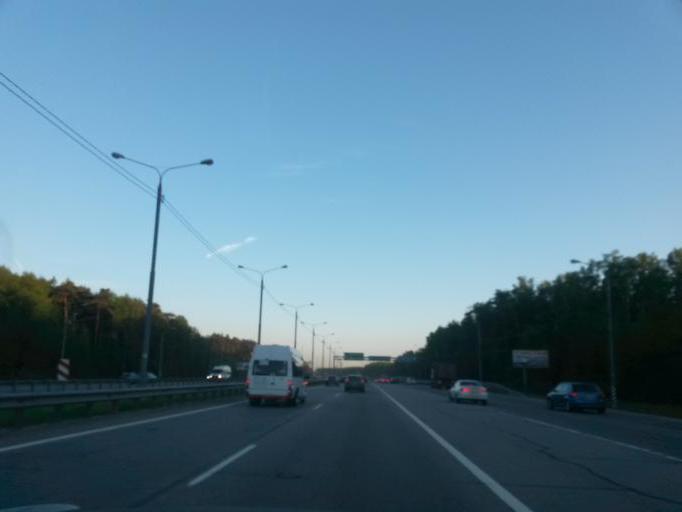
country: RU
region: Moskovskaya
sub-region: Podol'skiy Rayon
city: Podol'sk
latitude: 55.4131
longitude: 37.6078
